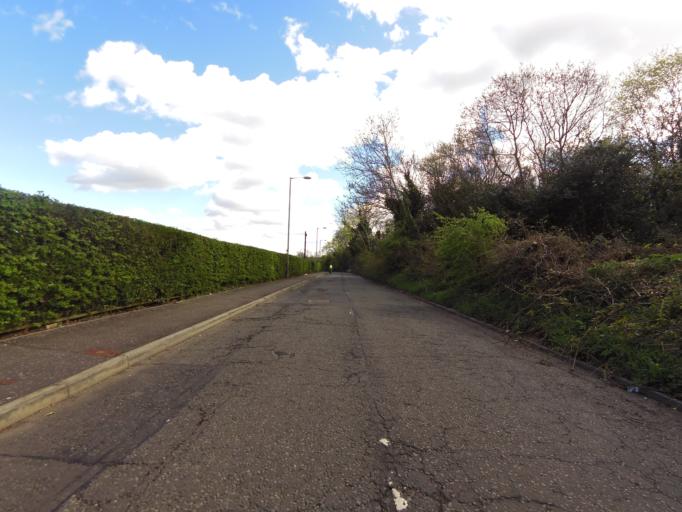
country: GB
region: Scotland
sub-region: West Lothian
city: Seafield
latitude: 55.9293
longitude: -3.1319
